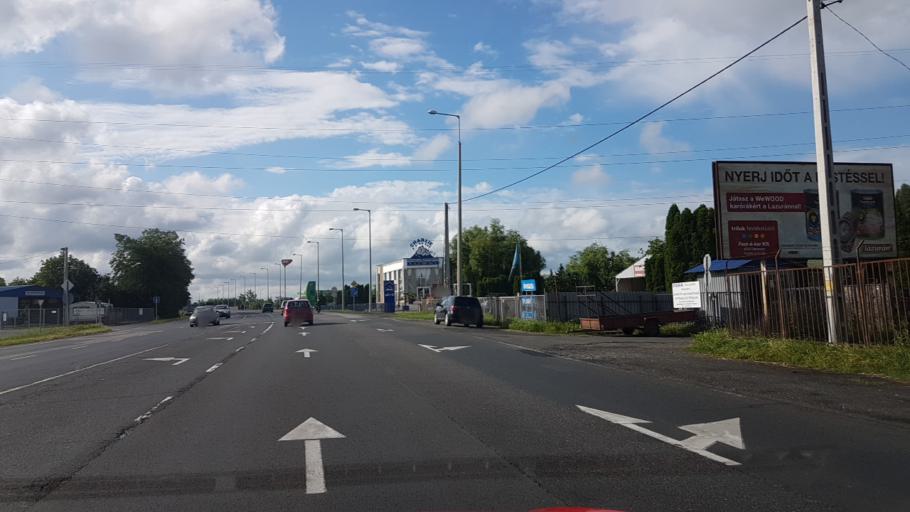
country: HU
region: Hajdu-Bihar
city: Debrecen
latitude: 47.5671
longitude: 21.5986
